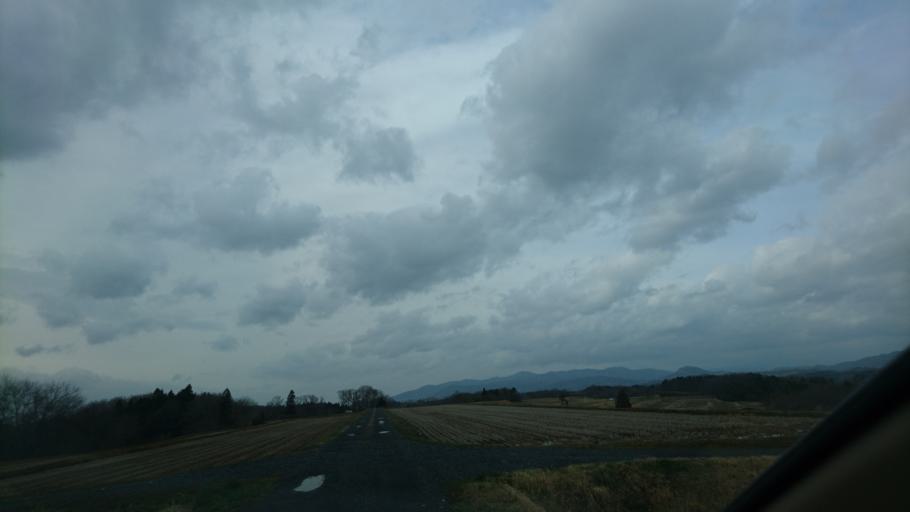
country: JP
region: Iwate
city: Ichinoseki
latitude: 38.8857
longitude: 141.1608
